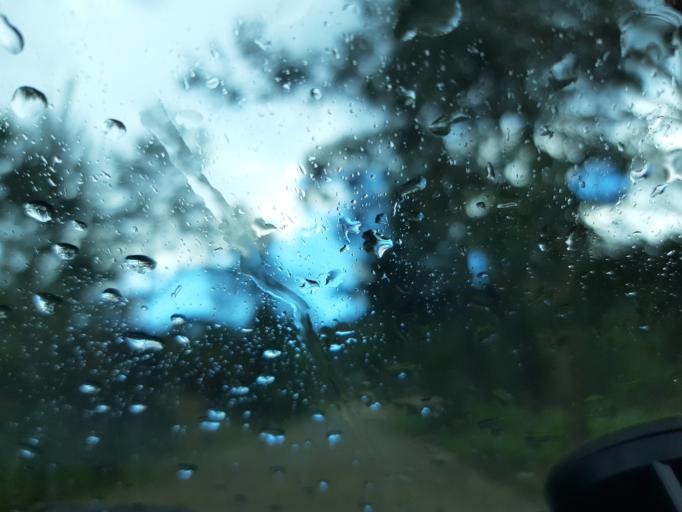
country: CO
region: Boyaca
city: Raquira
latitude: 5.4979
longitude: -73.6937
